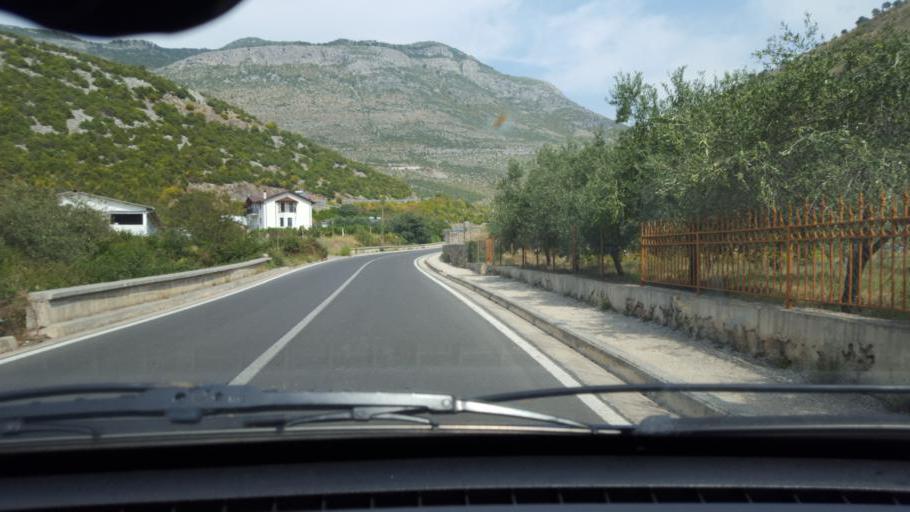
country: AL
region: Shkoder
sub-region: Rrethi i Malesia e Madhe
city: Hot
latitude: 42.3650
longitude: 19.4457
